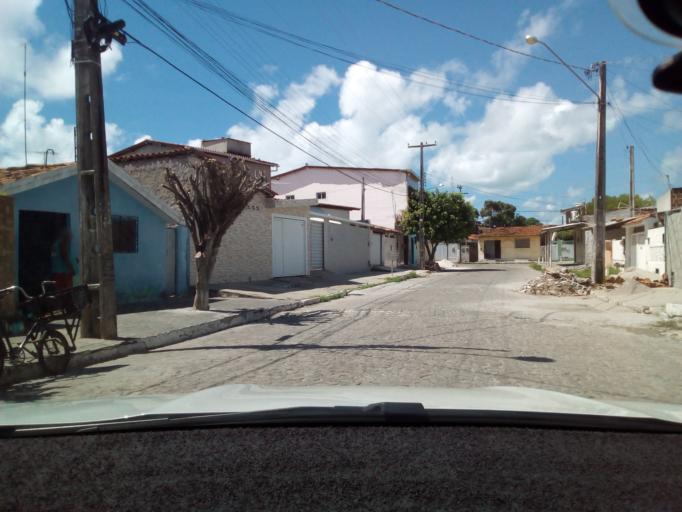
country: BR
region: Paraiba
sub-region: Cabedelo
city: Cabedelo
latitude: -6.9754
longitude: -34.8328
